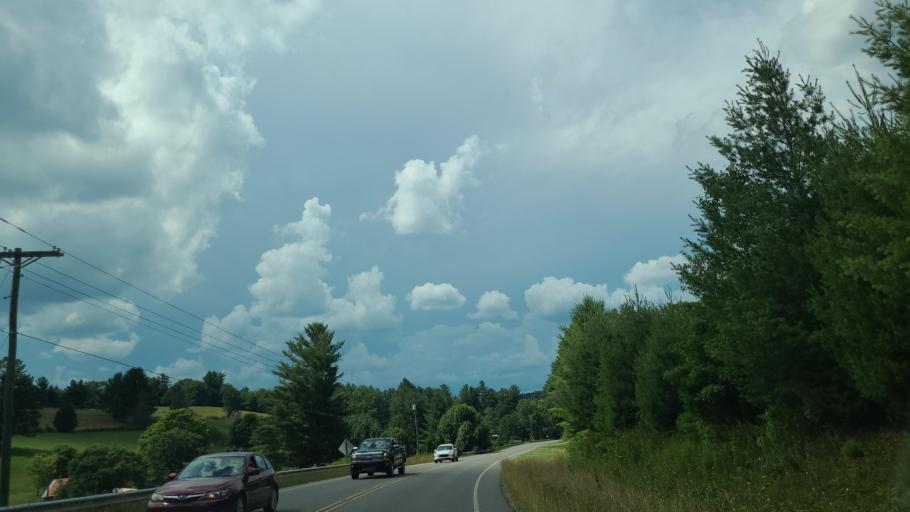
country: US
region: North Carolina
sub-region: Ashe County
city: Jefferson
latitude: 36.3521
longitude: -81.3858
